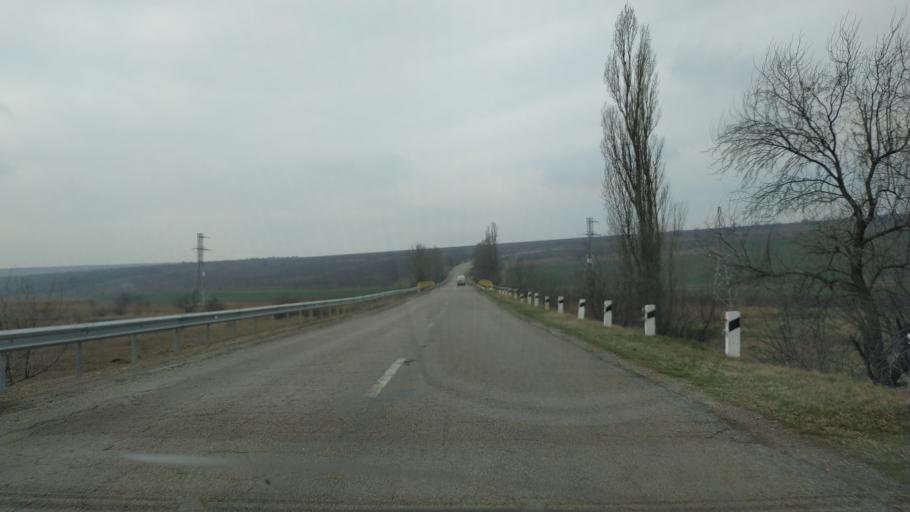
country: MD
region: Cahul
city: Cahul
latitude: 45.9568
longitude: 28.4056
